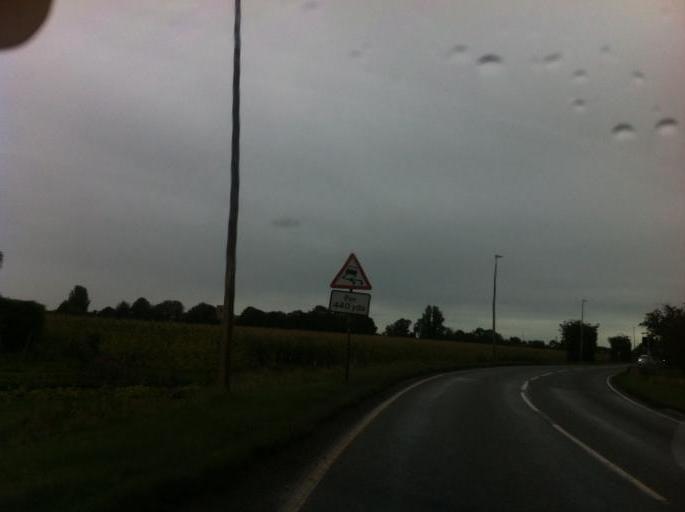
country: GB
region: England
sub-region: Lincolnshire
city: Boston
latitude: 52.9943
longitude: 0.0762
